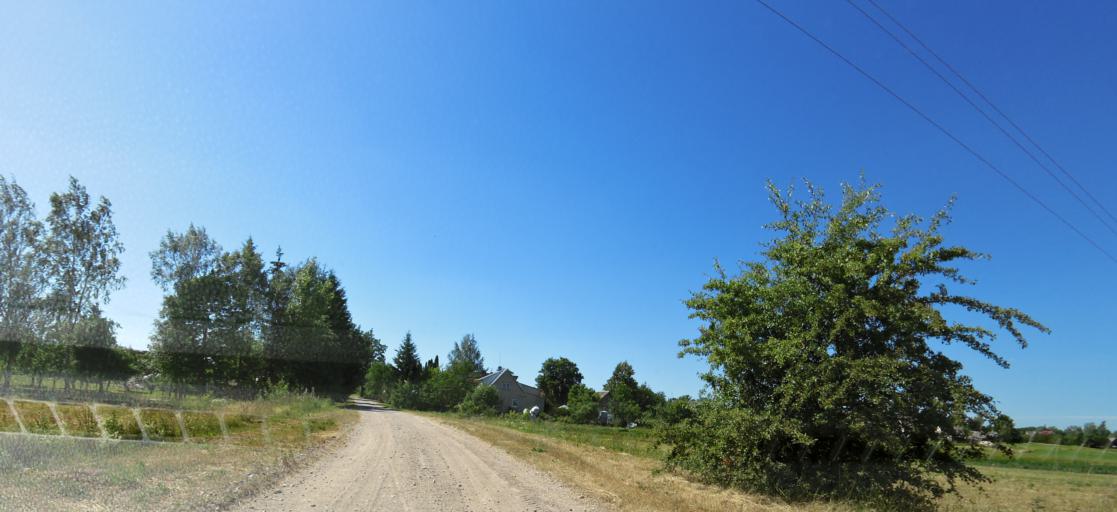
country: LT
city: Vabalninkas
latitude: 55.9819
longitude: 24.7571
